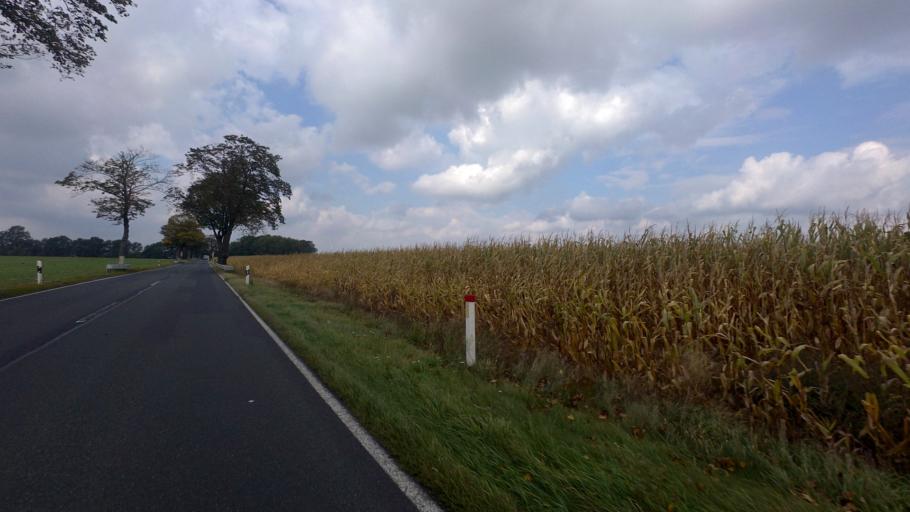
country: DE
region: Saxony-Anhalt
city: Holzdorf
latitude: 51.8076
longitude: 13.1690
